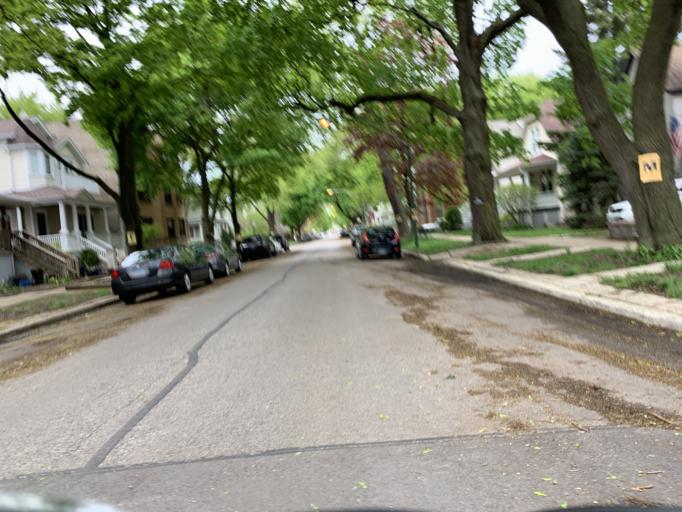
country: US
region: Illinois
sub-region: Cook County
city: Lincolnwood
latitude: 41.9660
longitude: -87.6815
